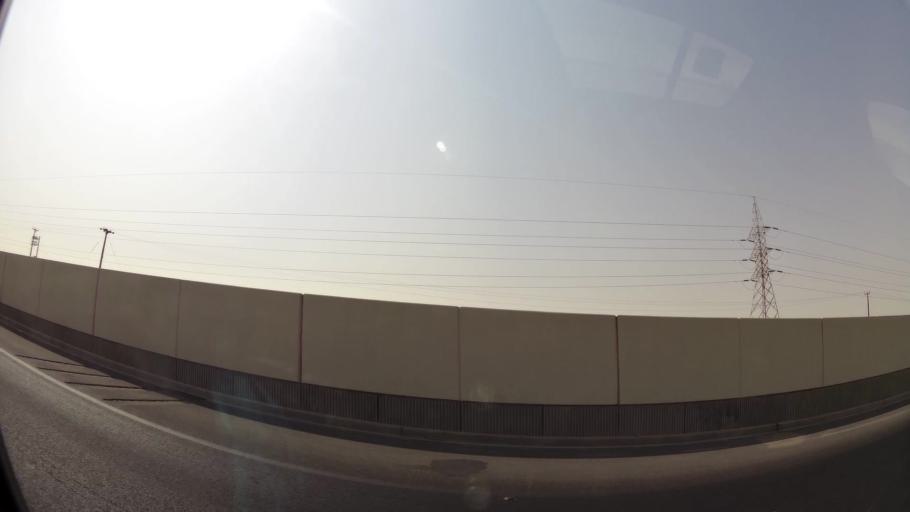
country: KW
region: Muhafazat al Jahra'
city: Al Jahra'
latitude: 29.3104
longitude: 47.6576
